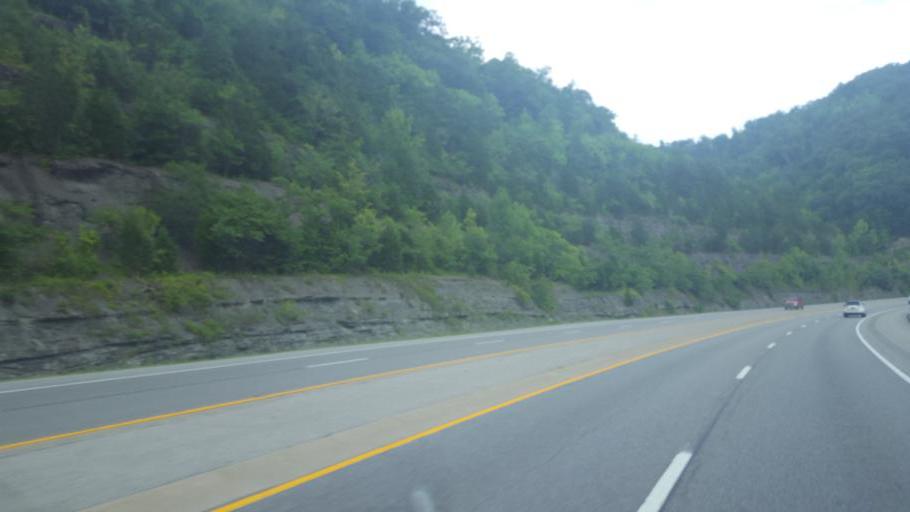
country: US
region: Kentucky
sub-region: Pike County
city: Pikeville
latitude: 37.4632
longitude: -82.5180
